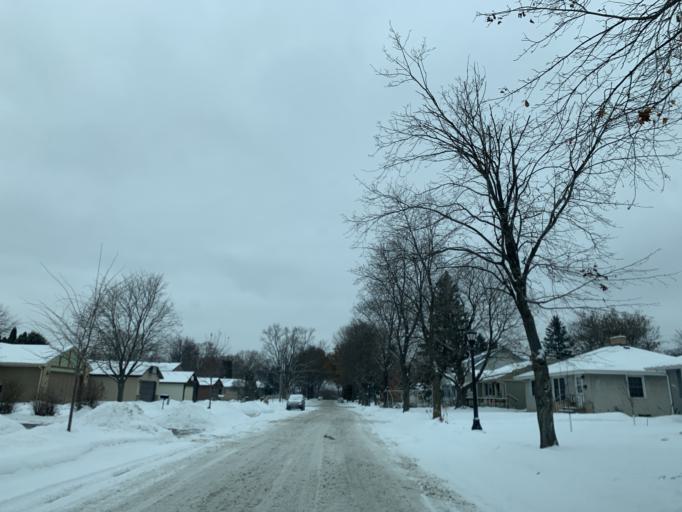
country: US
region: Minnesota
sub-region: Ramsey County
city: Roseville
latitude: 44.9855
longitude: -93.1173
